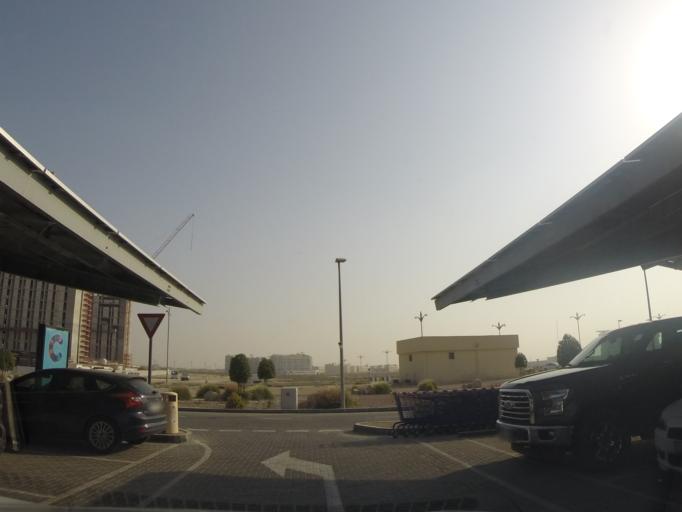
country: AE
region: Dubai
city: Dubai
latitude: 25.0396
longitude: 55.1969
